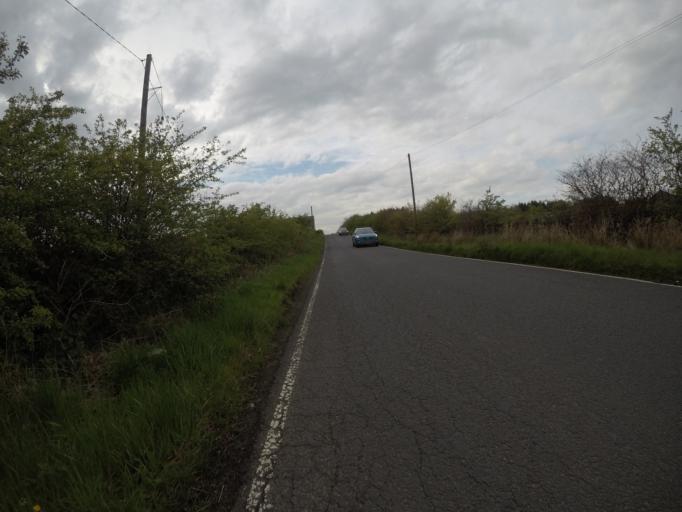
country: GB
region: Scotland
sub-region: East Ayrshire
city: Kilmarnock
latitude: 55.6422
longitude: -4.4786
